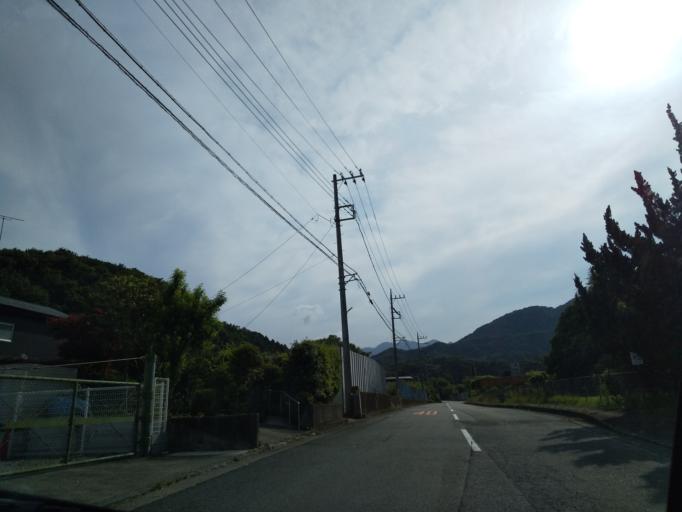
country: JP
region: Kanagawa
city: Atsugi
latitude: 35.4909
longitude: 139.3141
